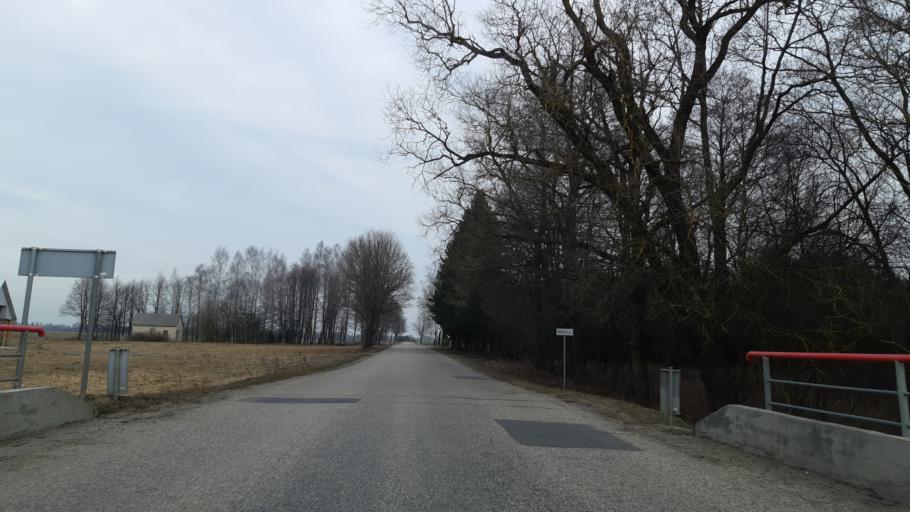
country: LT
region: Marijampoles apskritis
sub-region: Marijampole Municipality
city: Marijampole
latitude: 54.7132
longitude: 23.3183
